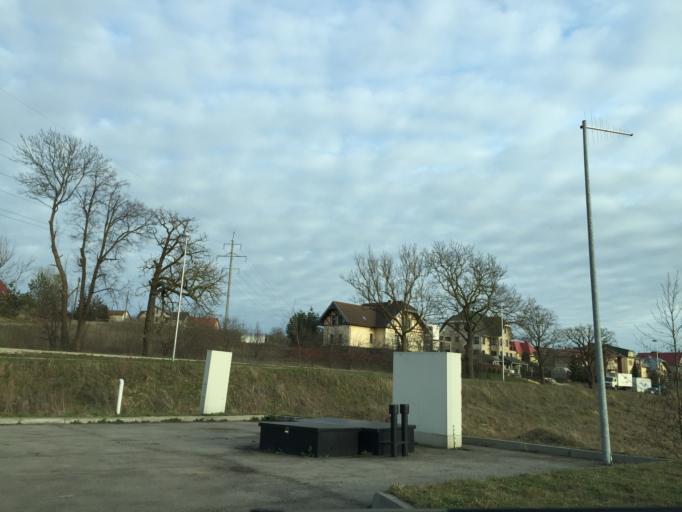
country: LT
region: Klaipedos apskritis
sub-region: Klaipeda
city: Klaipeda
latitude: 55.7216
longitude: 21.1693
